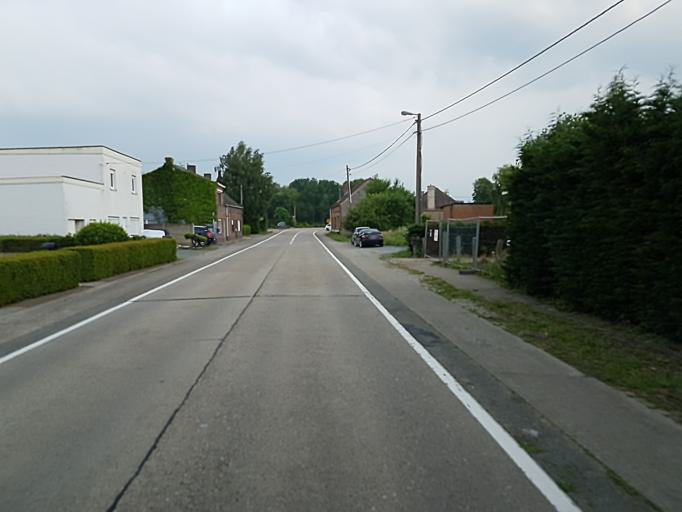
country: BE
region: Flanders
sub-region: Provincie Antwerpen
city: Putte
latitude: 51.0750
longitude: 4.6549
